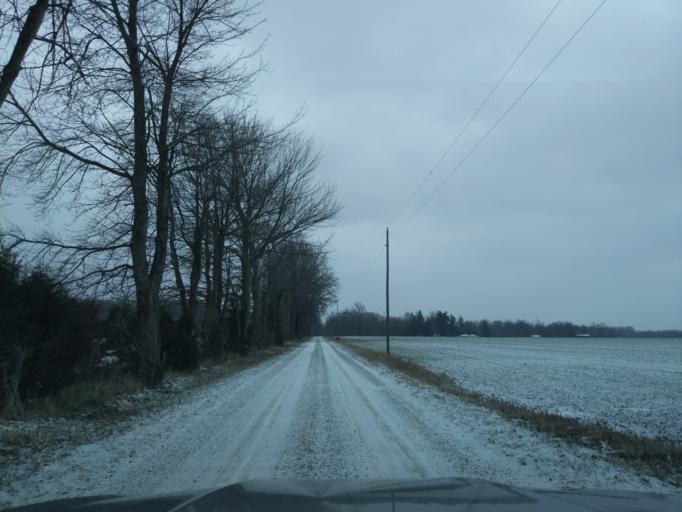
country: US
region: Indiana
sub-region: Decatur County
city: Westport
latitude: 39.2045
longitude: -85.4575
